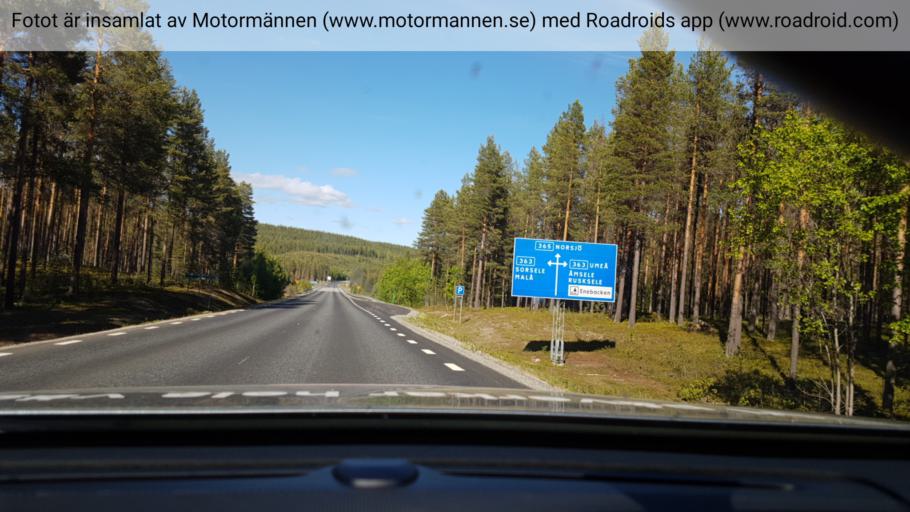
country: SE
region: Vaesterbotten
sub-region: Lycksele Kommun
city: Lycksele
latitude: 64.8213
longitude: 18.7900
